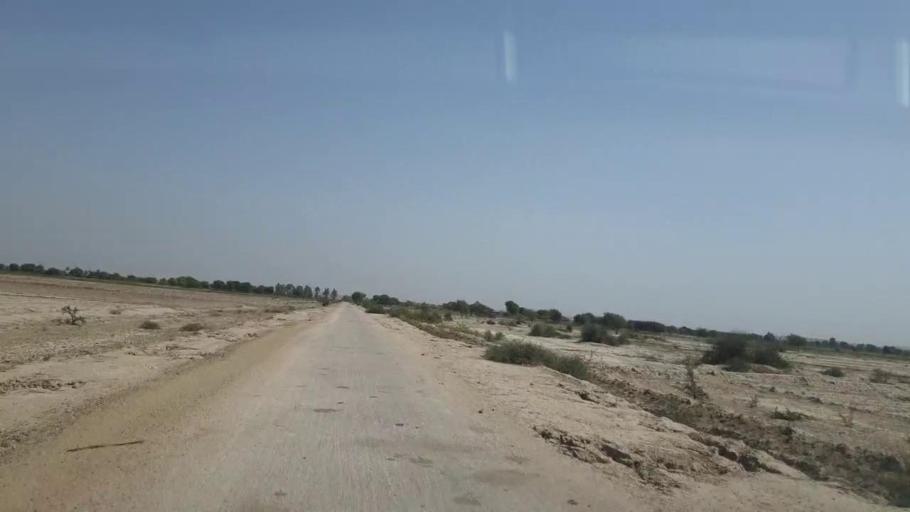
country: PK
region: Sindh
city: Naukot
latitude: 24.9309
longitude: 69.4943
